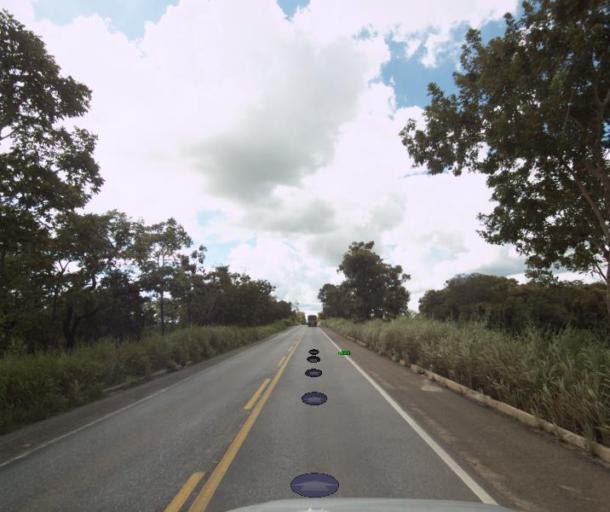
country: BR
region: Goias
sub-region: Porangatu
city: Porangatu
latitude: -13.2997
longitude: -49.1216
